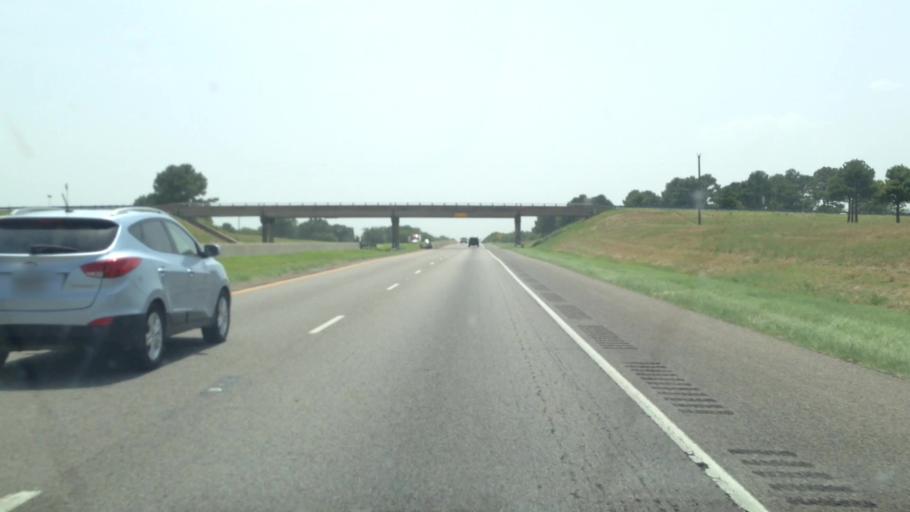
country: US
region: Texas
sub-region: Franklin County
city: Mount Vernon
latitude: 33.1626
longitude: -95.4038
